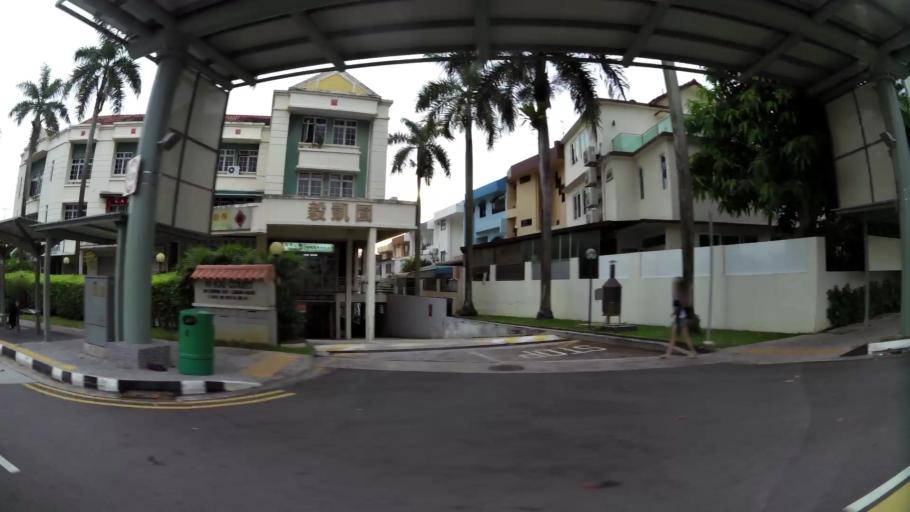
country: SG
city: Singapore
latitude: 1.3485
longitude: 103.8802
